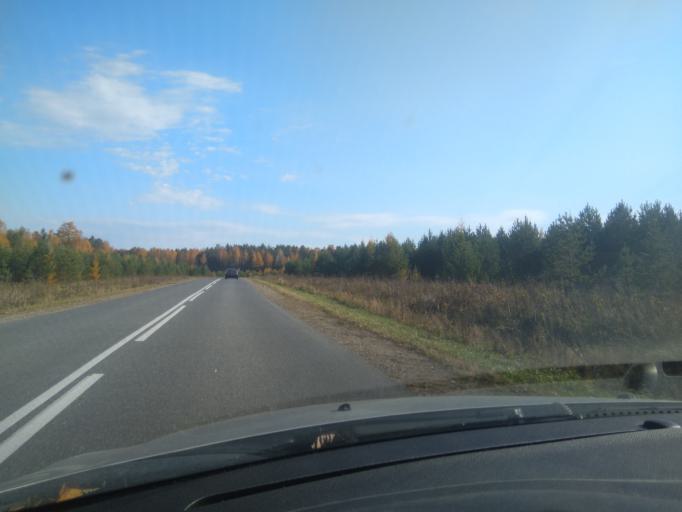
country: RU
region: Sverdlovsk
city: Mikhaylovsk
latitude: 56.5329
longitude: 59.2123
